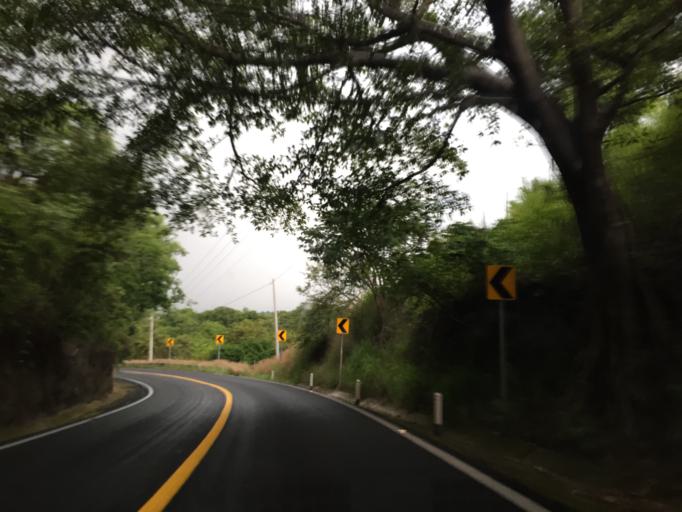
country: MX
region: Colima
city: Cuauhtemoc
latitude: 19.3444
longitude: -103.5814
